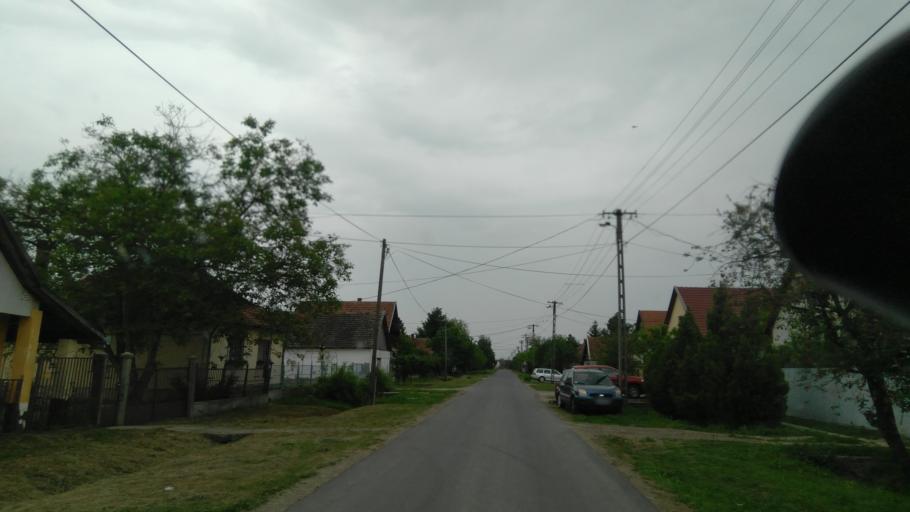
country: HU
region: Bekes
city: Doboz
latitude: 46.7294
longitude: 21.2484
